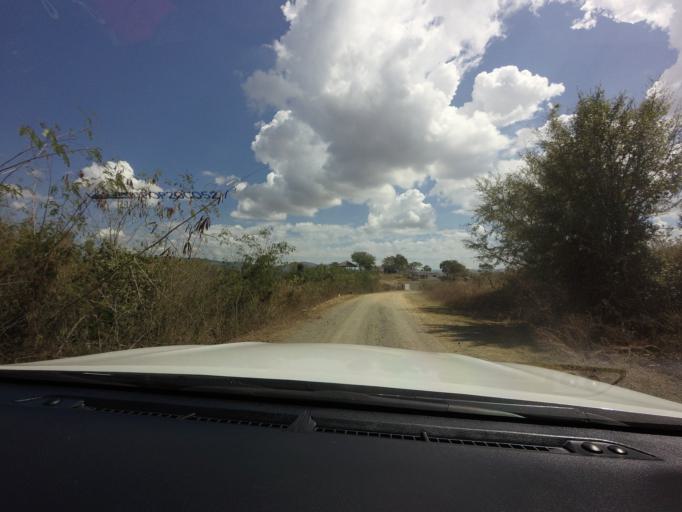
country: TH
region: Nakhon Ratchasima
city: Wang Nam Khiao
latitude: 14.4668
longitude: 101.7730
